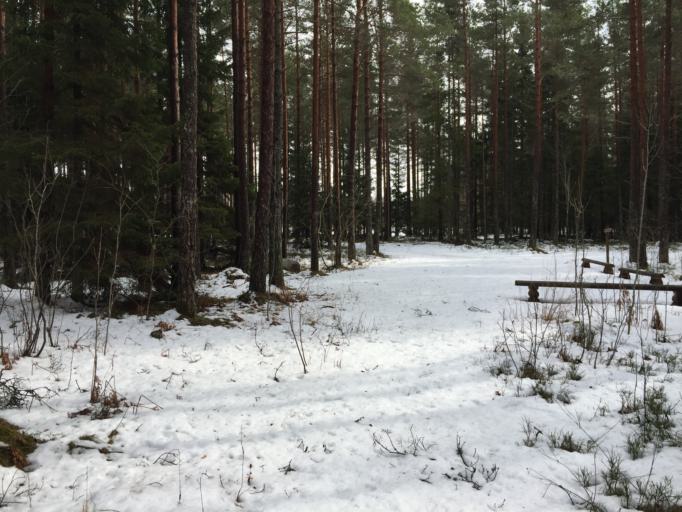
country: EE
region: Saare
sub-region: Kuressaare linn
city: Kuressaare
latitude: 58.3957
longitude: 22.1634
